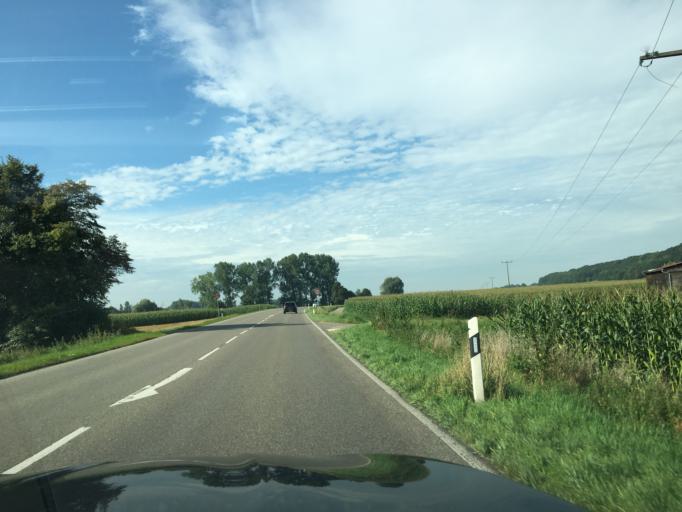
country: DE
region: Baden-Wuerttemberg
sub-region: Tuebingen Region
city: Ersingen
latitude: 48.3109
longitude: 9.8607
